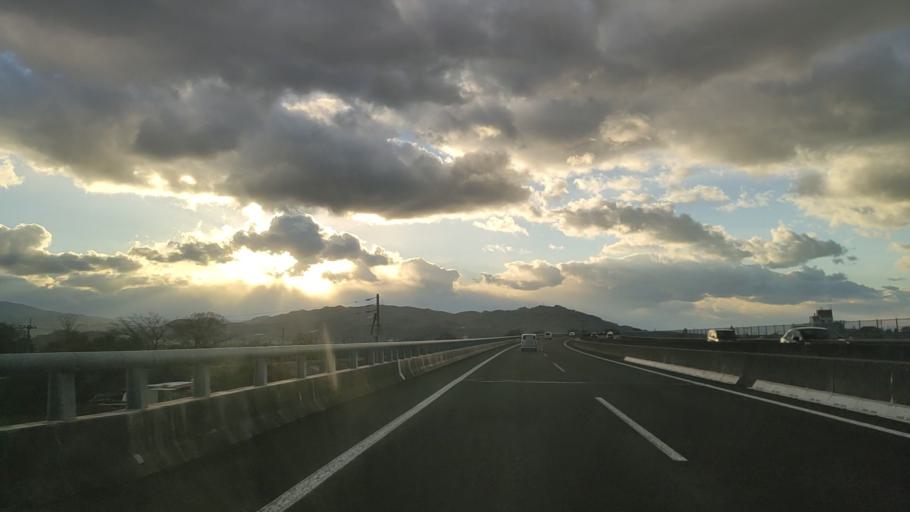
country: JP
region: Ehime
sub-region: Shikoku-chuo Shi
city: Matsuyama
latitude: 33.7880
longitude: 132.8198
